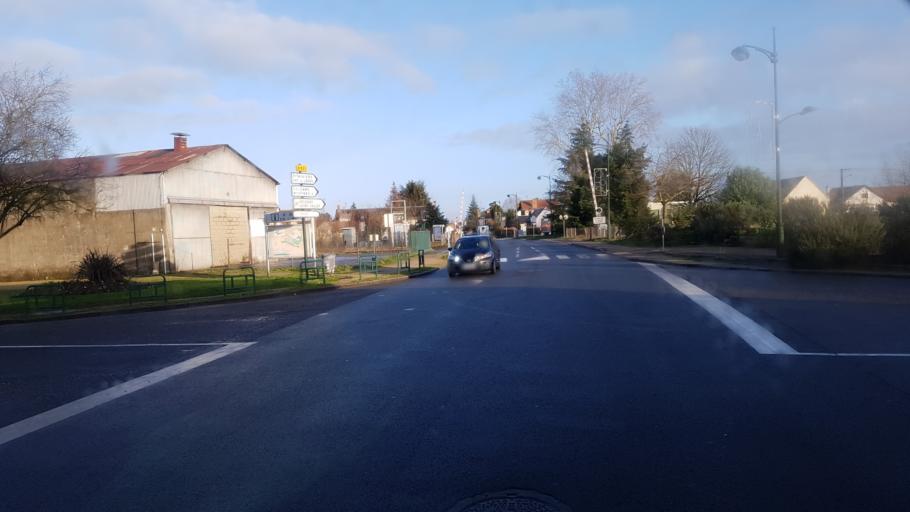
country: FR
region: Centre
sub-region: Departement du Loiret
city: Jargeau
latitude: 47.8737
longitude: 2.1274
